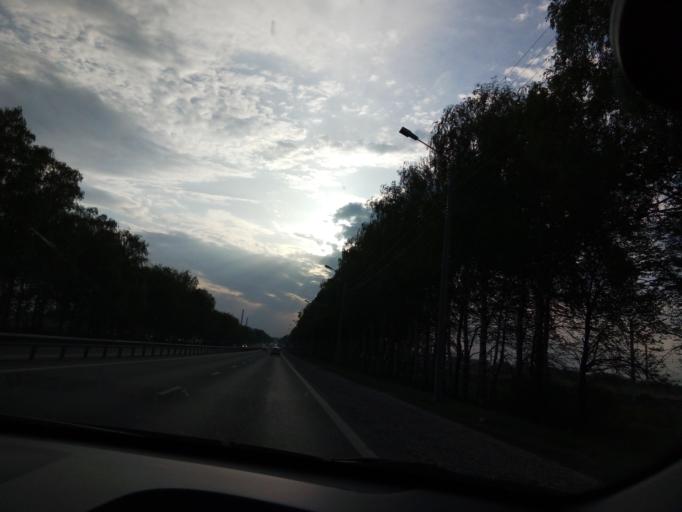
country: RU
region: Chuvashia
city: Novocheboksarsk
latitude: 56.1253
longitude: 47.3718
